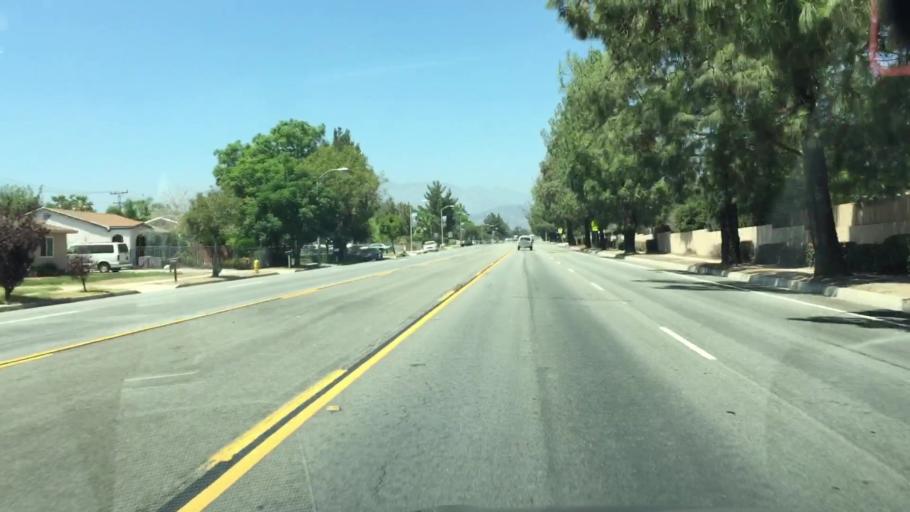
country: US
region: California
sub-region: San Bernardino County
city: Muscoy
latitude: 34.1735
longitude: -117.3252
